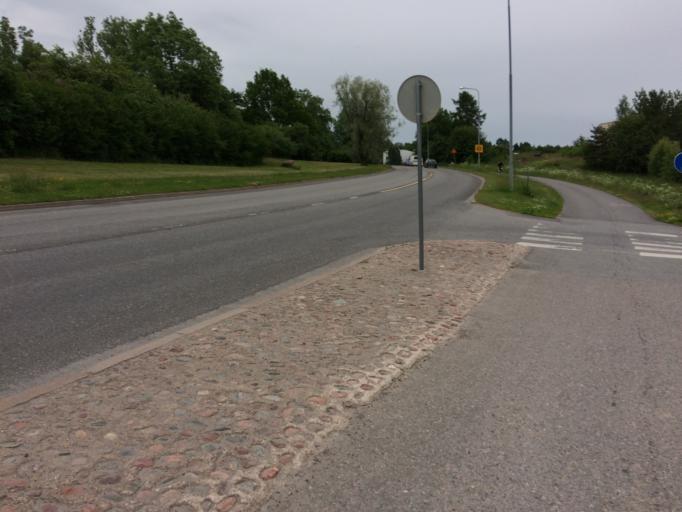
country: FI
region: Varsinais-Suomi
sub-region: Turku
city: Turku
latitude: 60.4639
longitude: 22.3035
